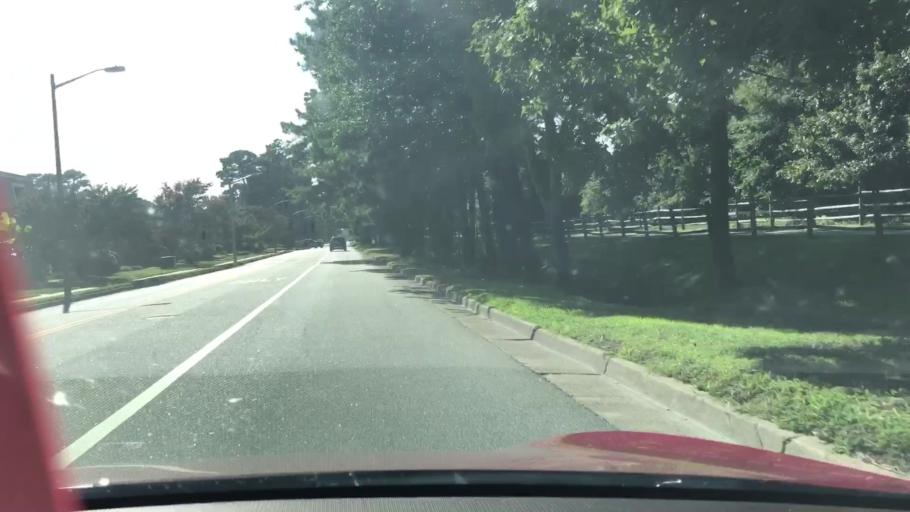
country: US
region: Virginia
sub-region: City of Virginia Beach
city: Virginia Beach
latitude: 36.8378
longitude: -75.9884
